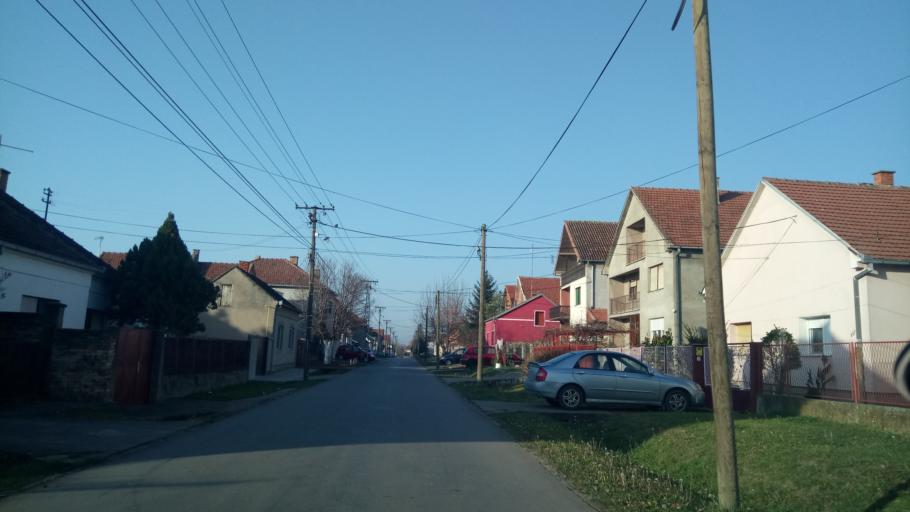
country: RS
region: Autonomna Pokrajina Vojvodina
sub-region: Sremski Okrug
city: Stara Pazova
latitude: 44.9842
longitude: 20.1754
